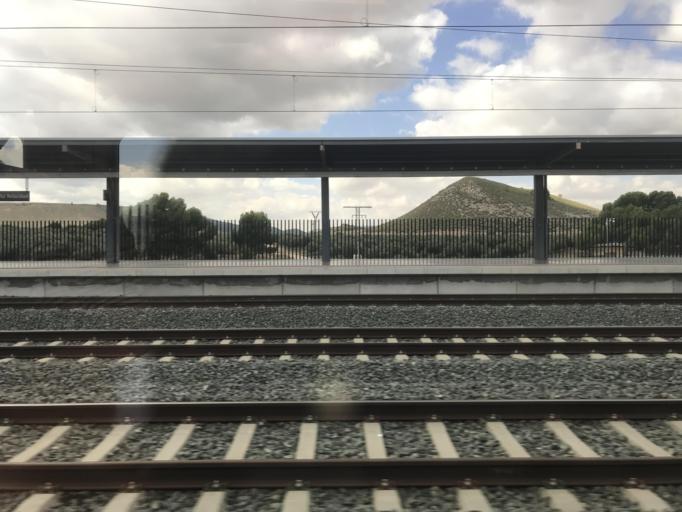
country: ES
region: Valencia
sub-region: Provincia de Alicante
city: Villena
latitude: 38.5857
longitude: -0.8743
